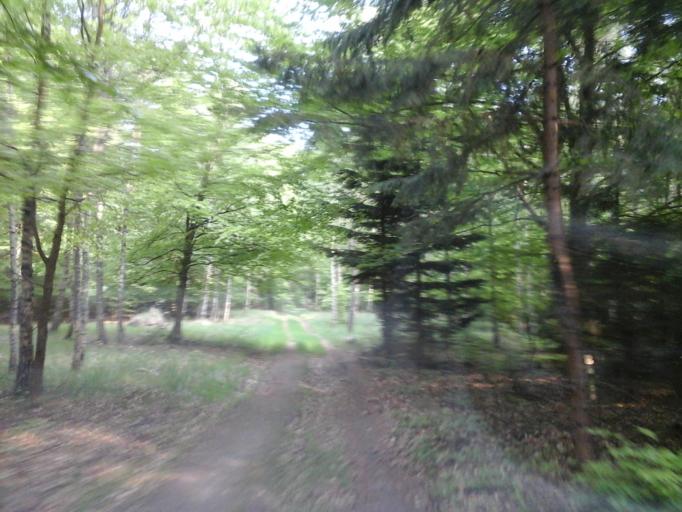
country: PL
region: West Pomeranian Voivodeship
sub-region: Powiat choszczenski
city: Pelczyce
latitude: 52.9597
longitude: 15.3653
